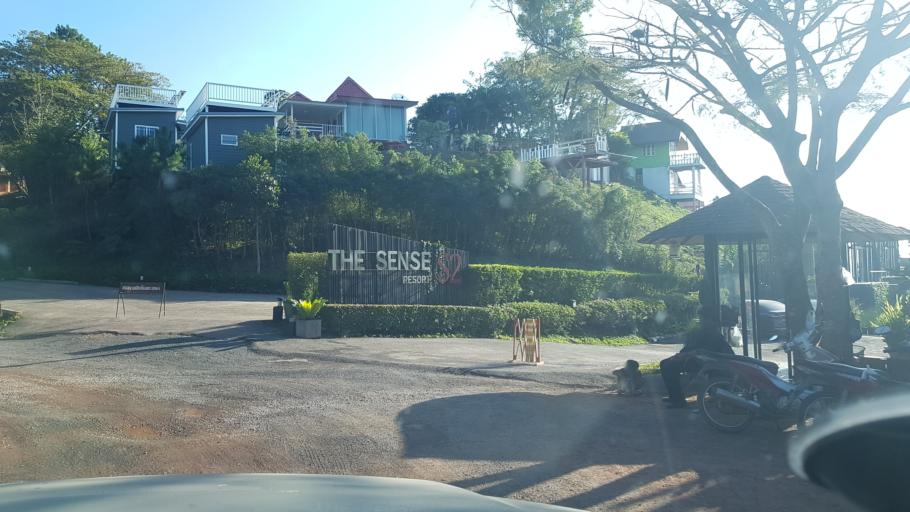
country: TH
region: Phetchabun
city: Khao Kho
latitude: 16.6473
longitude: 100.9999
